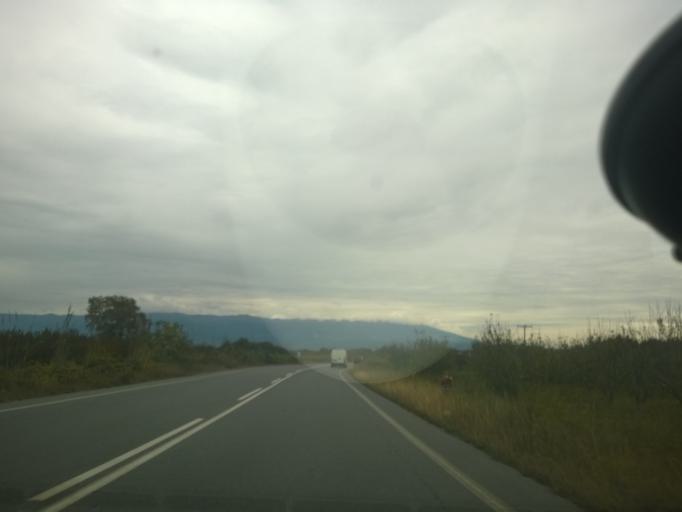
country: GR
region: Central Macedonia
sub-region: Nomos Pellis
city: Loutraki
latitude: 40.9723
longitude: 21.9736
